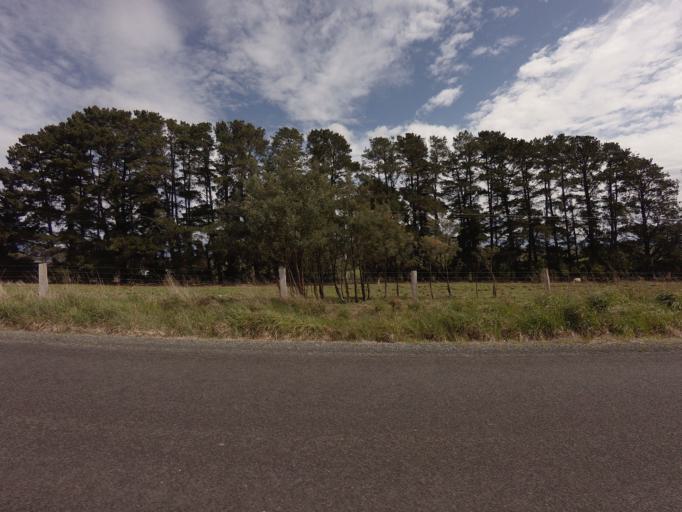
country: AU
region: Tasmania
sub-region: Northern Midlands
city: Longford
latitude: -41.7629
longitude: 147.2101
